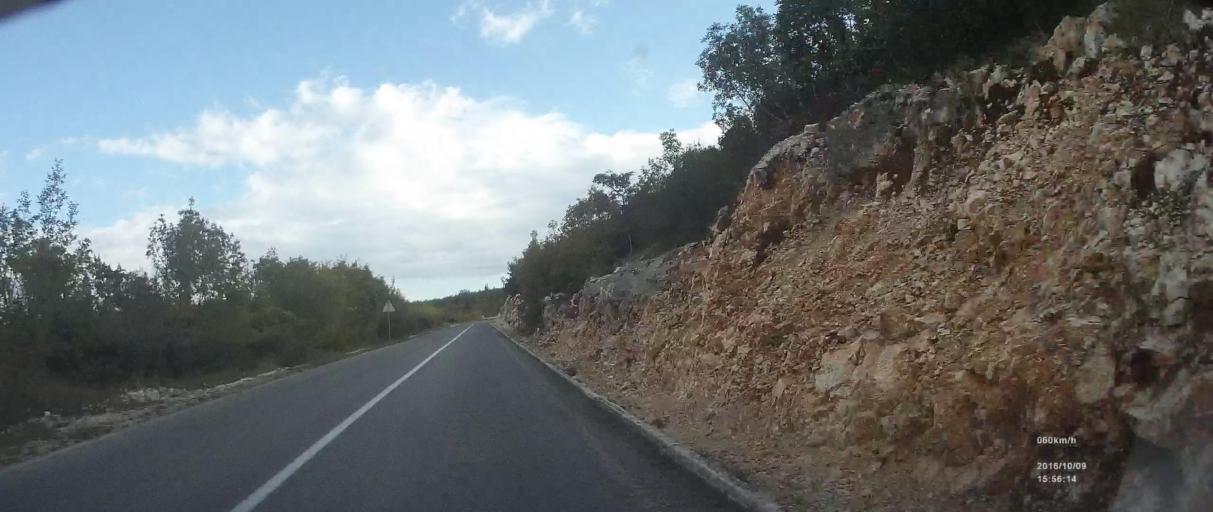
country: HR
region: Splitsko-Dalmatinska
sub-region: Grad Trogir
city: Trogir
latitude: 43.5798
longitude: 16.2323
